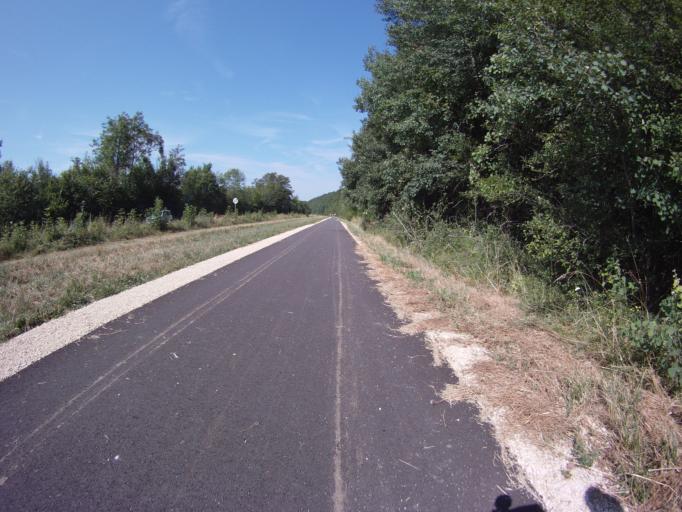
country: FR
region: Lorraine
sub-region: Departement de Meurthe-et-Moselle
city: Liverdun
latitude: 48.7570
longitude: 6.0263
